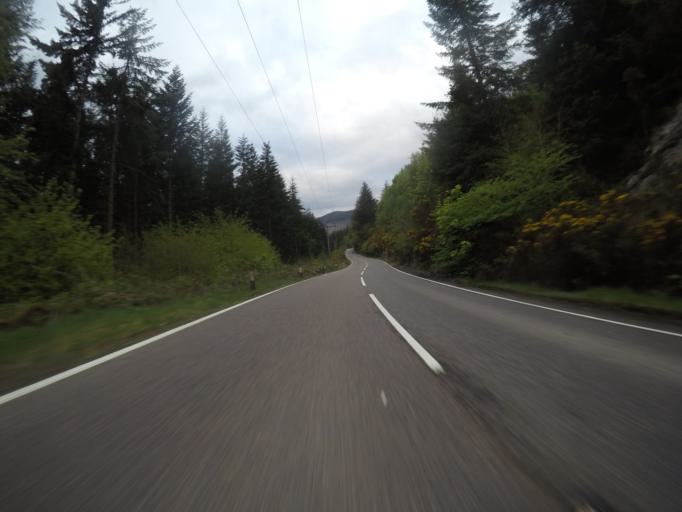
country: GB
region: Scotland
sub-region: Highland
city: Beauly
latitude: 57.2167
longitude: -4.5871
